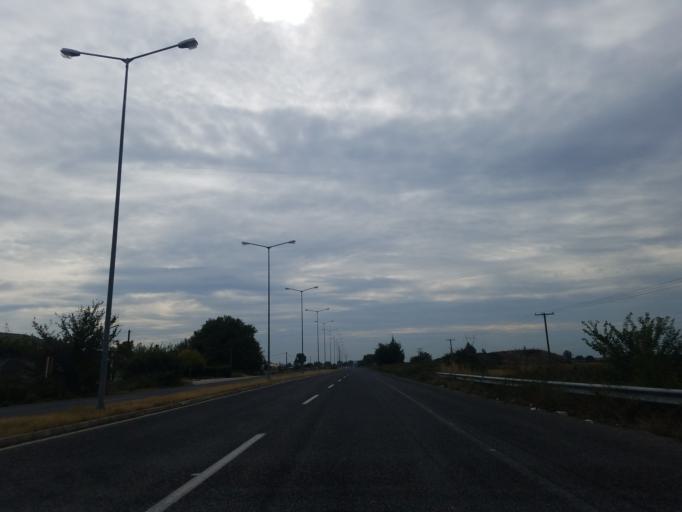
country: GR
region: Thessaly
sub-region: Trikala
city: Vasiliki
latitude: 39.6325
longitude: 21.7014
